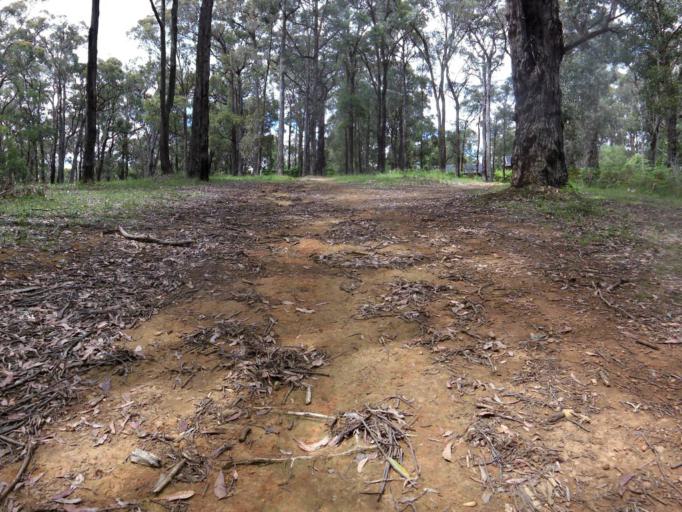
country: AU
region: Victoria
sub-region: Cardinia
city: Cockatoo
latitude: -37.9389
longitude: 145.4753
